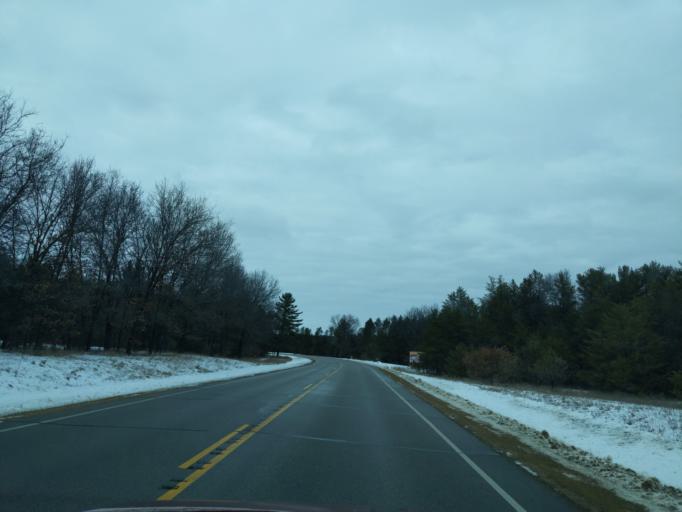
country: US
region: Wisconsin
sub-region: Waushara County
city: Wautoma
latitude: 43.9545
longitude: -89.3174
